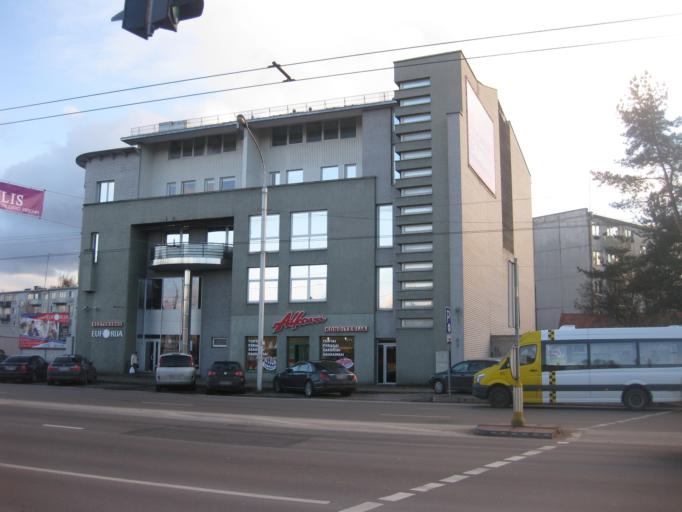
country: LT
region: Kauno apskritis
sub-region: Kaunas
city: Silainiai
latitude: 54.9152
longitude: 23.8925
